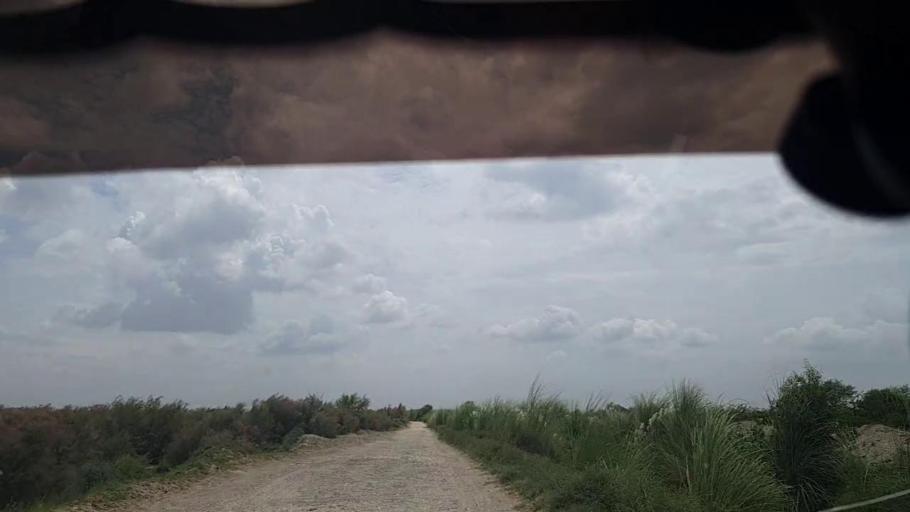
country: PK
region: Sindh
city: Rustam jo Goth
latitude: 28.0520
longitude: 68.9393
